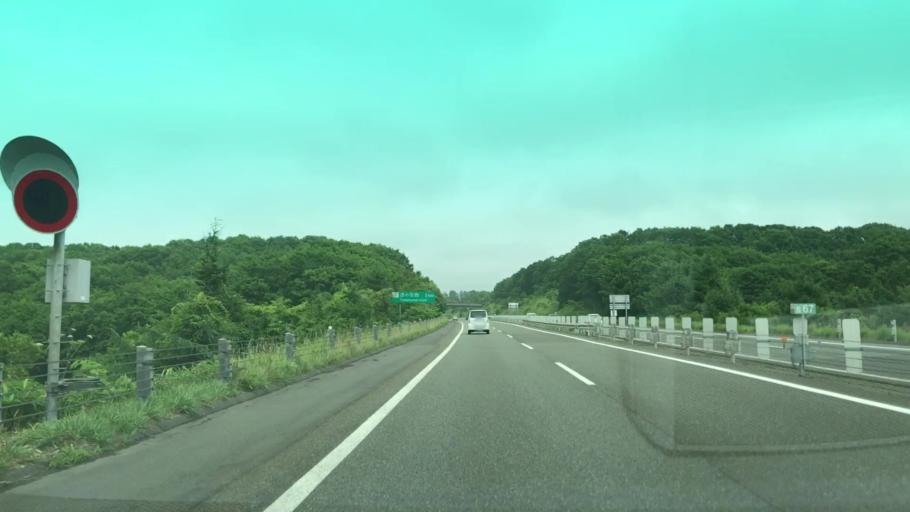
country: JP
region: Hokkaido
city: Tomakomai
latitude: 42.6179
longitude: 141.4738
